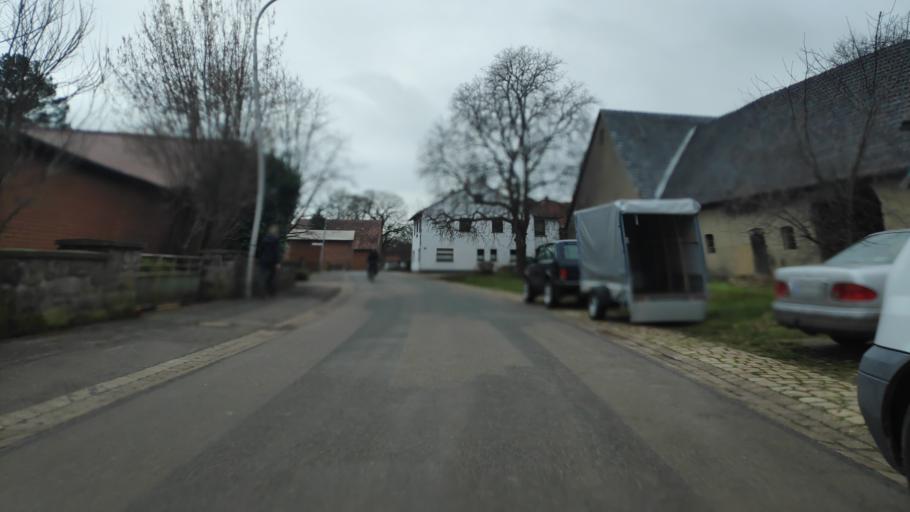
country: DE
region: North Rhine-Westphalia
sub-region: Regierungsbezirk Detmold
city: Minden
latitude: 52.3035
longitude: 8.8486
